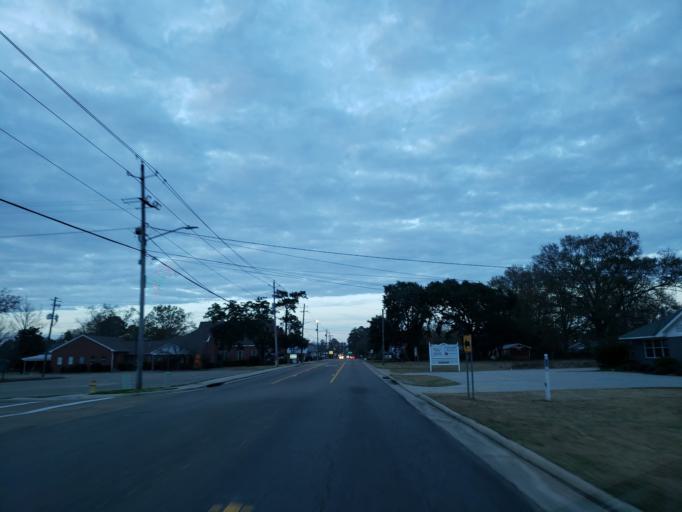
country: US
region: Mississippi
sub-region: Forrest County
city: Petal
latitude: 31.3392
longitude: -89.2629
